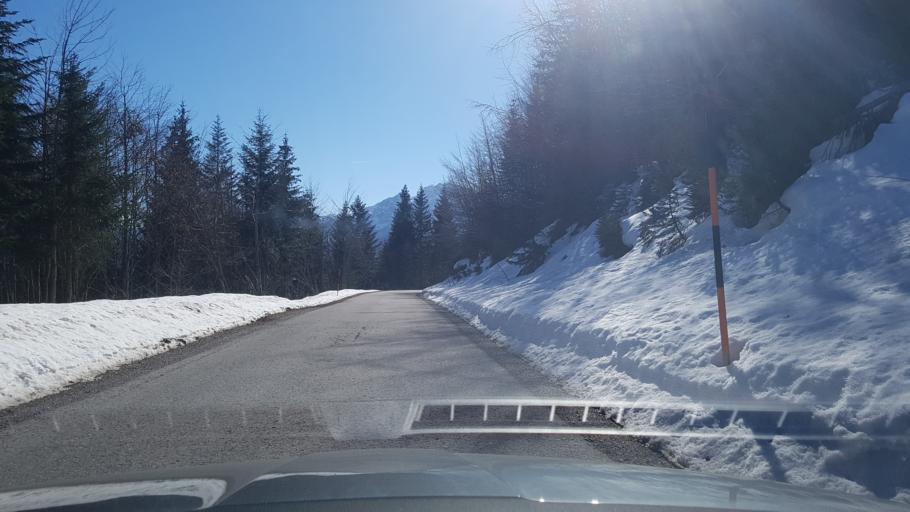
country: AT
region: Salzburg
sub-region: Politischer Bezirk Hallein
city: Abtenau
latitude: 47.6106
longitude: 13.3856
